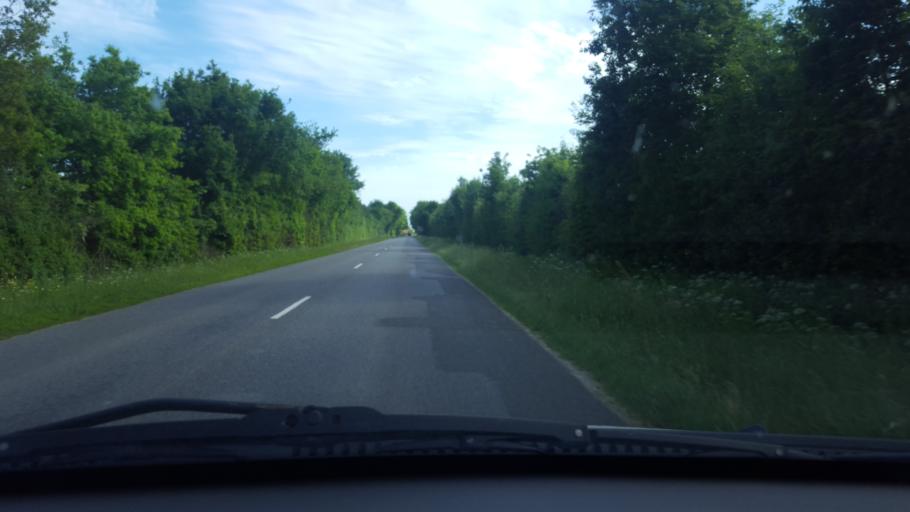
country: FR
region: Pays de la Loire
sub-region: Departement de la Loire-Atlantique
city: La Chevroliere
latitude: 47.0686
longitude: -1.5676
